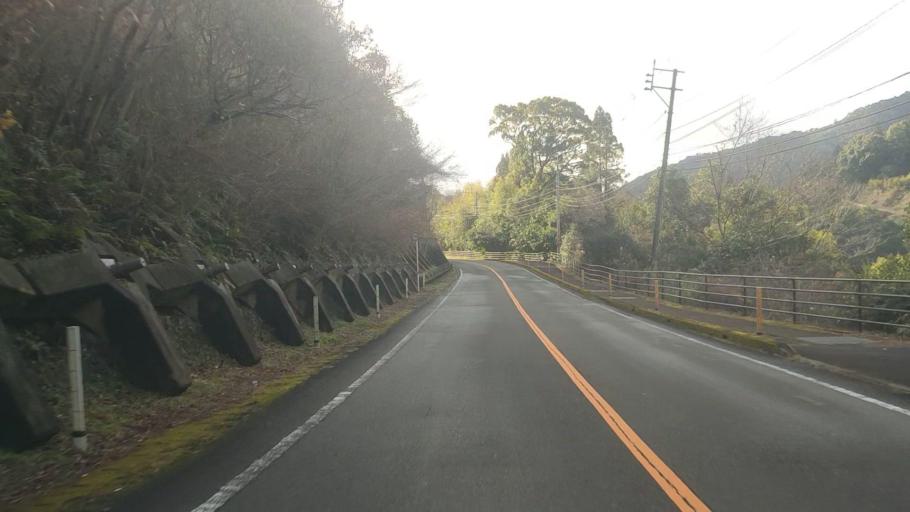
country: JP
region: Kumamoto
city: Hitoyoshi
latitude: 32.3105
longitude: 130.8478
